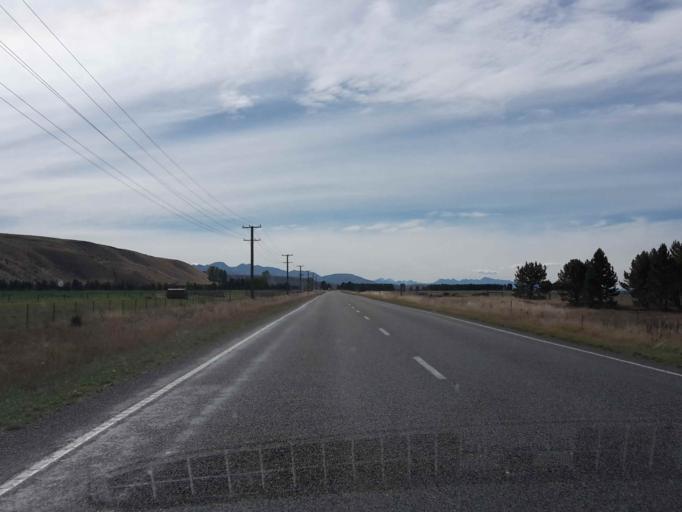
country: NZ
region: Otago
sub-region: Queenstown-Lakes District
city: Wanaka
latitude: -44.3798
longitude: 169.9985
